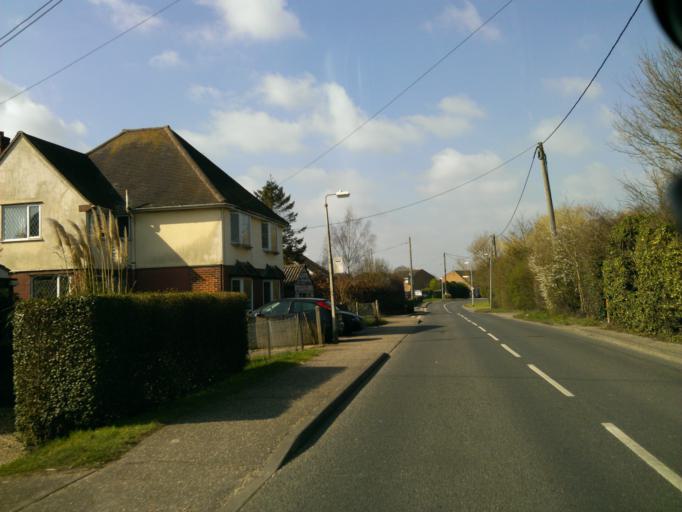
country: GB
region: England
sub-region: Essex
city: Witham
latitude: 51.8432
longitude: 0.6325
